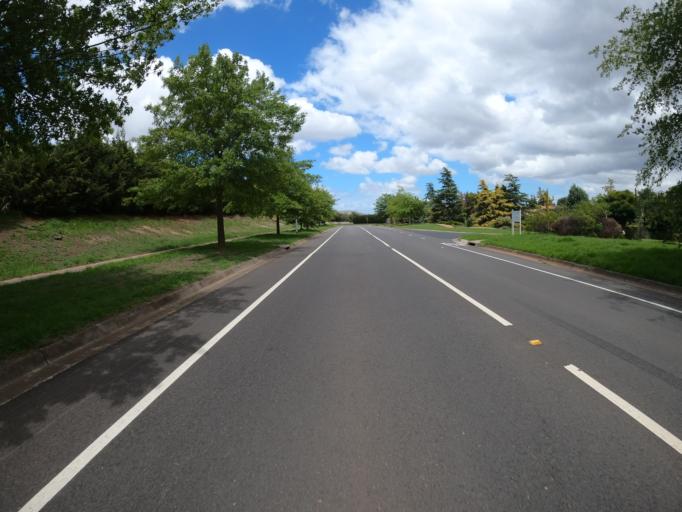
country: AU
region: Victoria
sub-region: Hume
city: Attwood
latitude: -37.6596
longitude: 144.8994
